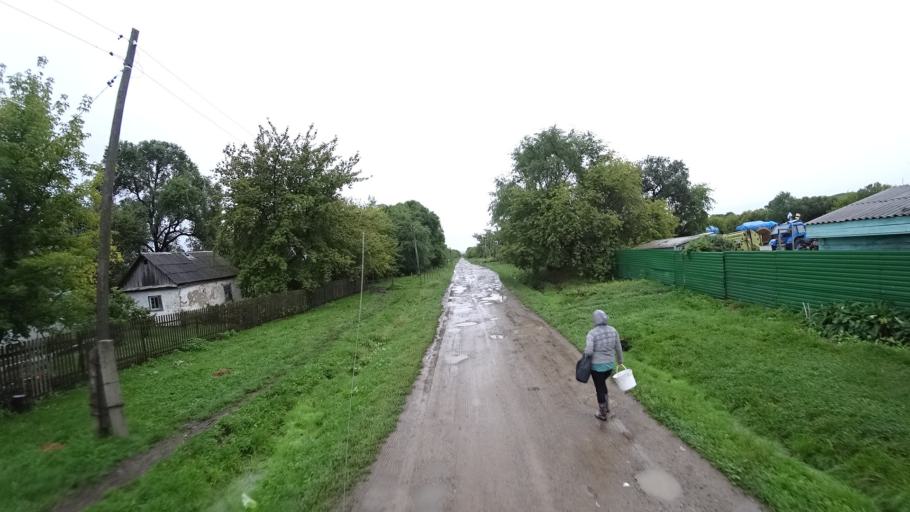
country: RU
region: Primorskiy
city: Monastyrishche
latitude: 44.2546
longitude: 132.4269
